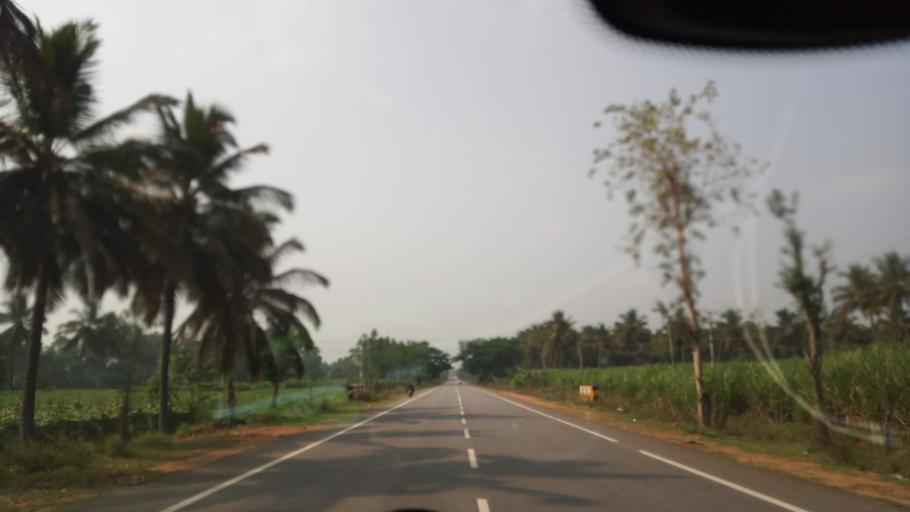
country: IN
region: Karnataka
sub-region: Mandya
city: Pandavapura
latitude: 12.5373
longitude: 76.6703
